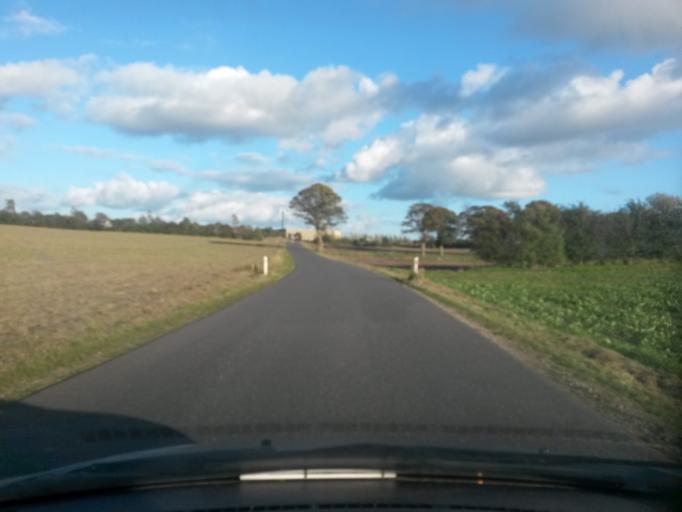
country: DK
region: Central Jutland
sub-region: Viborg Kommune
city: Viborg
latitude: 56.3744
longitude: 9.3833
